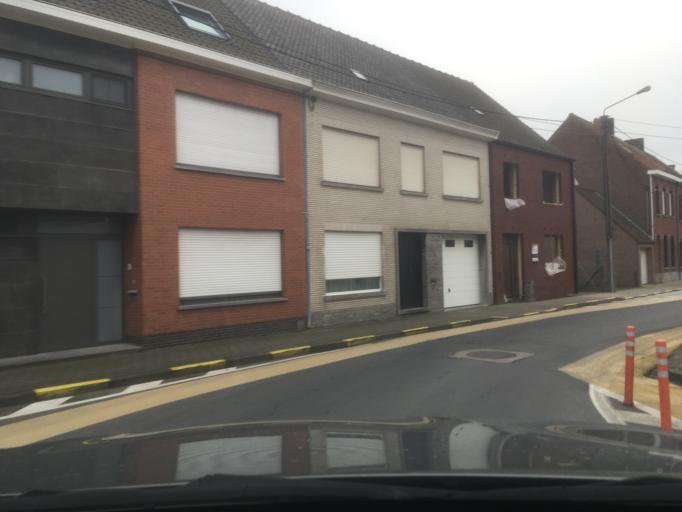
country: BE
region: Flanders
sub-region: Provincie West-Vlaanderen
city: Zwevegem
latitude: 50.8141
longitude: 3.3475
